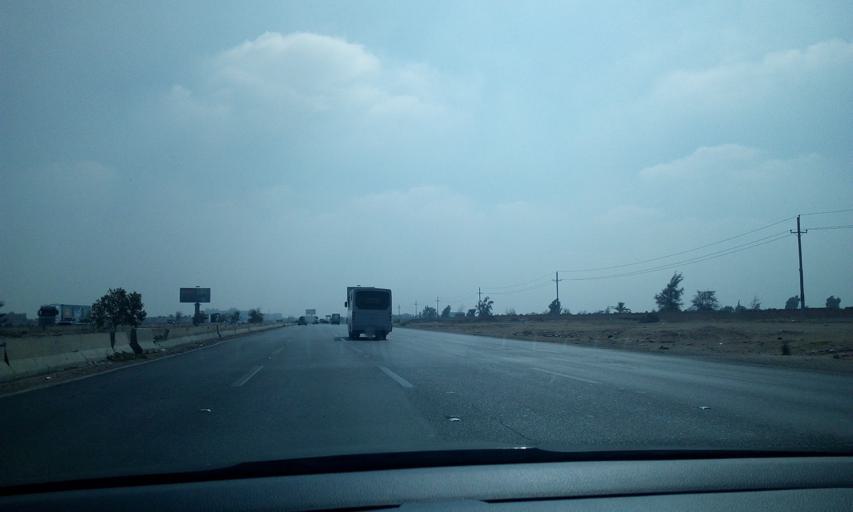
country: EG
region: Eastern Province
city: Bilbays
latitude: 30.1876
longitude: 31.6357
